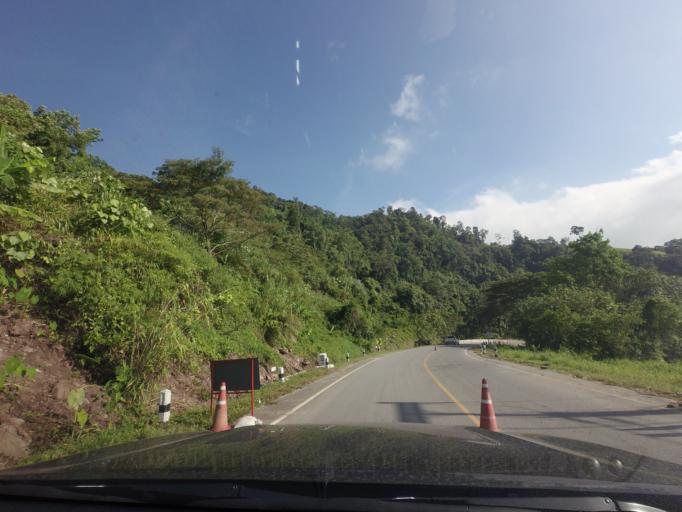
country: TH
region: Phetchabun
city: Lom Kao
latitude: 16.8870
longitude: 101.1204
